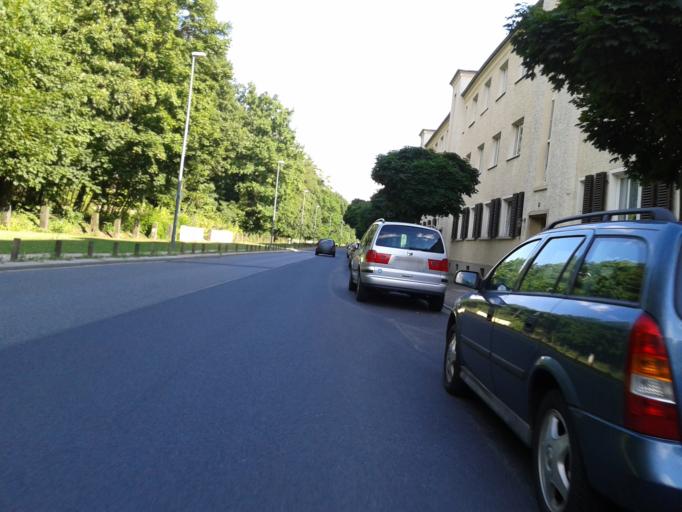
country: DE
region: Saxony
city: Albertstadt
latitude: 51.0844
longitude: 13.7429
